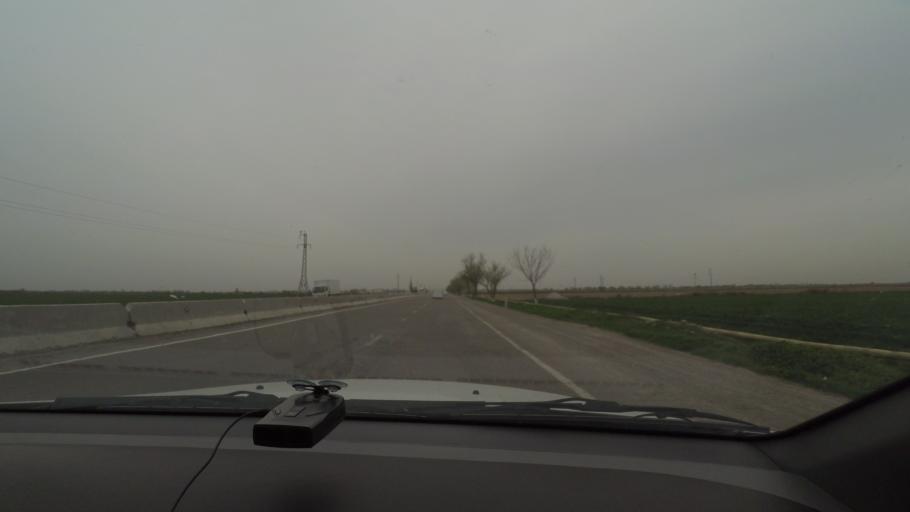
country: KZ
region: Ongtustik Qazaqstan
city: Myrzakent
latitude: 40.5579
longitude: 68.3880
